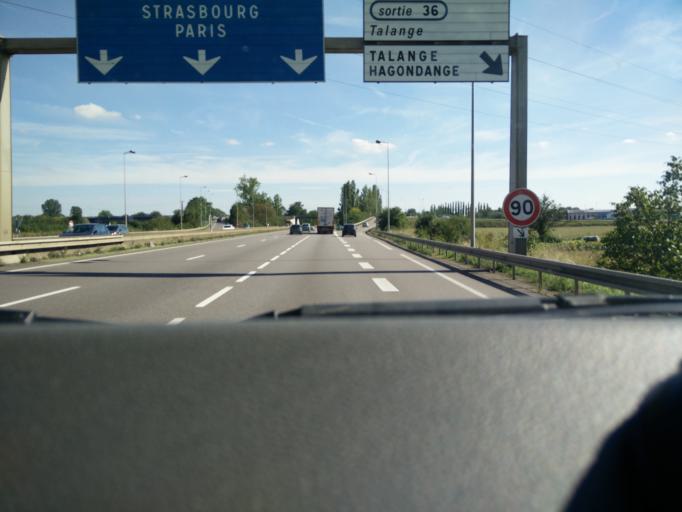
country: FR
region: Lorraine
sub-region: Departement de la Moselle
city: Talange
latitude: 49.2446
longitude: 6.1783
